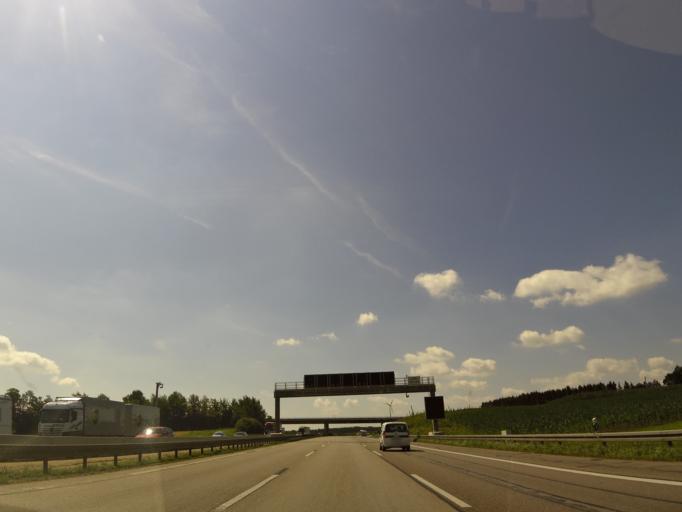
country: DE
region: Bavaria
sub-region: Upper Bavaria
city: Schweitenkirchen
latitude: 48.5391
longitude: 11.5949
